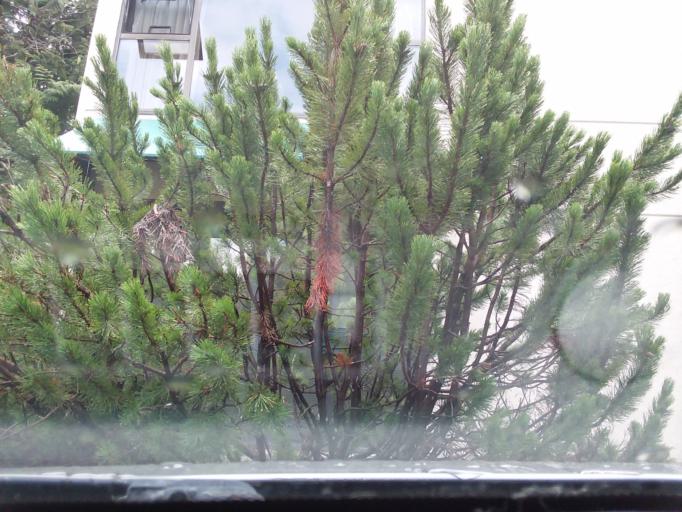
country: CA
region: British Columbia
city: Whistler
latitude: 50.0875
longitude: -122.9983
